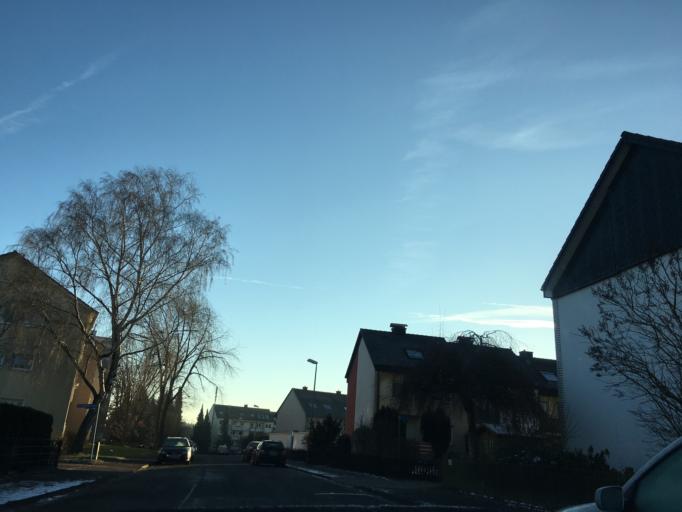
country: DE
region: North Rhine-Westphalia
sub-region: Regierungsbezirk Detmold
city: Detmold
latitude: 51.9426
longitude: 8.8299
